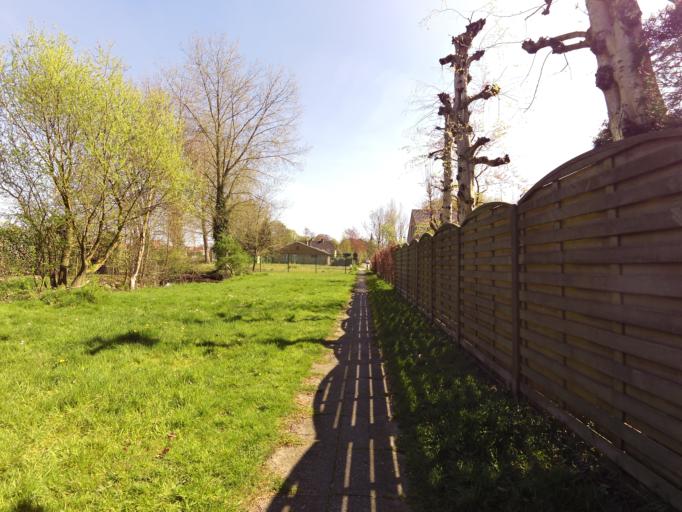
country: BE
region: Flanders
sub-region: Provincie West-Vlaanderen
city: Jabbeke
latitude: 51.1869
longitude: 3.0898
